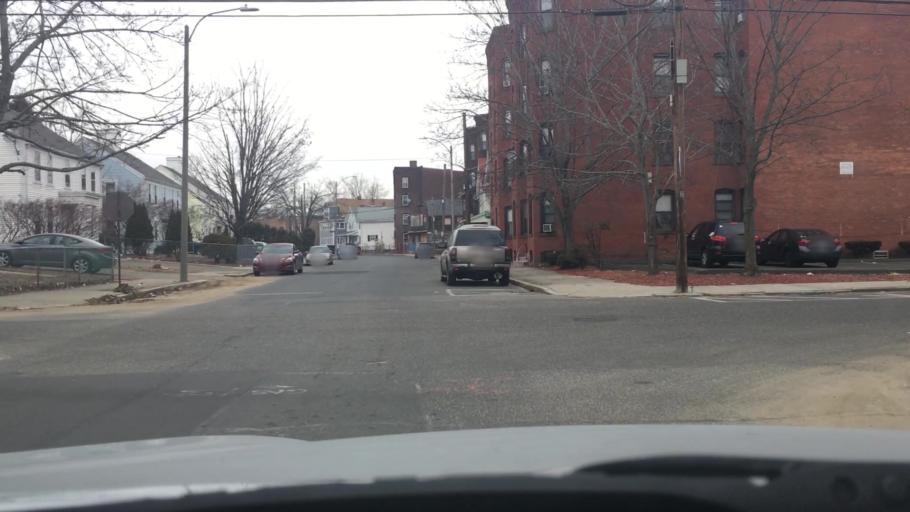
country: US
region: Massachusetts
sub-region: Hampden County
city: Holyoke
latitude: 42.2046
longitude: -72.5968
